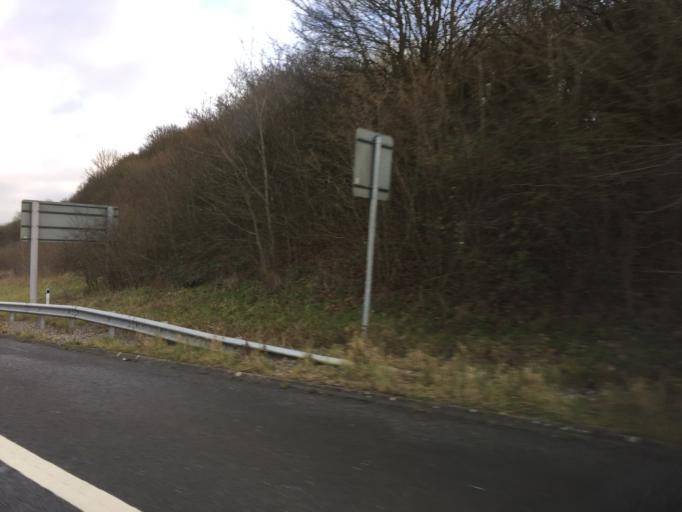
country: GB
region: England
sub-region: South Gloucestershire
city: Falfield
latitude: 51.6375
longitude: -2.4505
